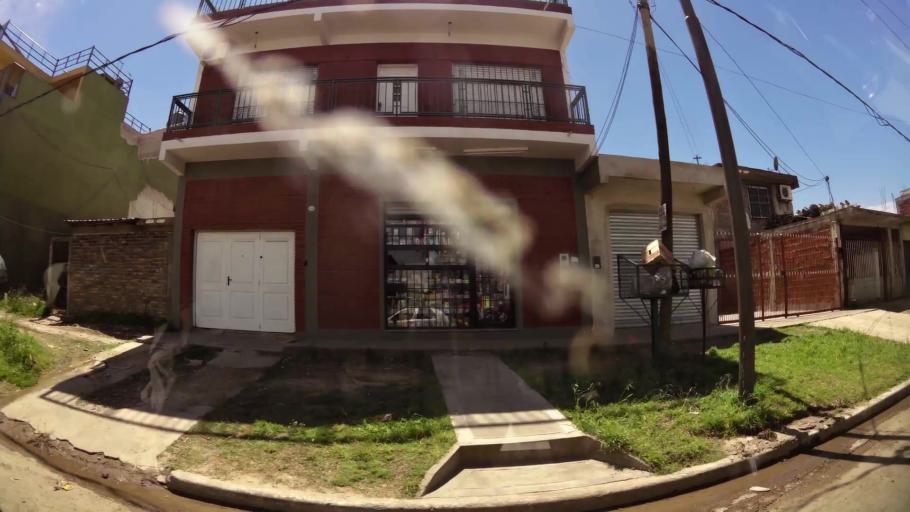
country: AR
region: Buenos Aires
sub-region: Partido de Quilmes
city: Quilmes
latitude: -34.7415
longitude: -58.3069
